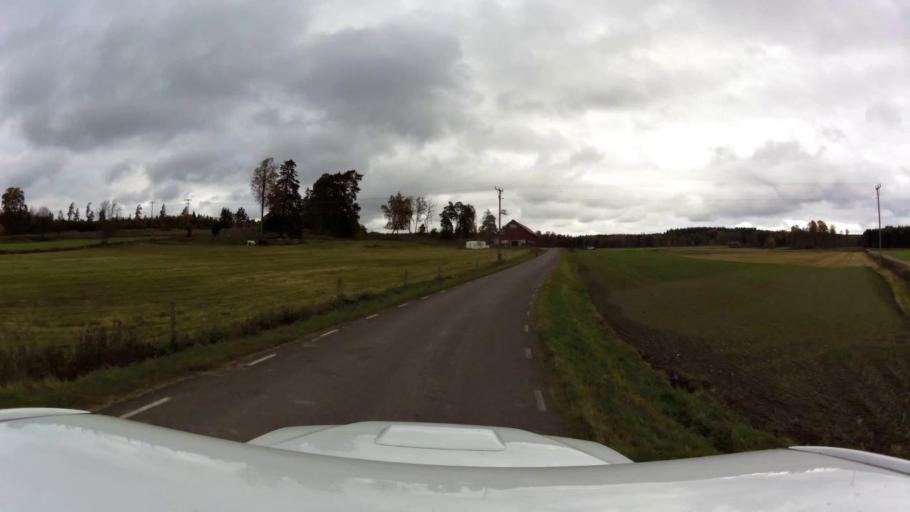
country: SE
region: OEstergoetland
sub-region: Motala Kommun
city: Borensberg
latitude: 58.5681
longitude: 15.3881
